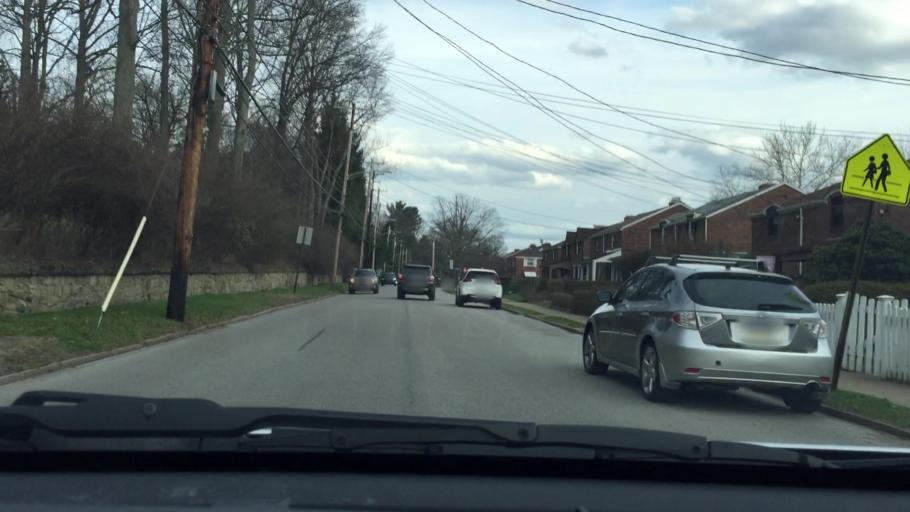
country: US
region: Pennsylvania
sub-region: Allegheny County
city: Leetsdale
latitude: 40.5636
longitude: -80.2051
